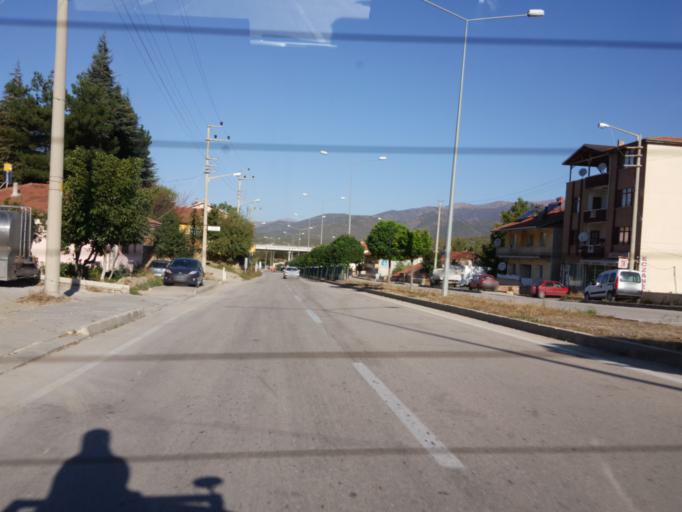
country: TR
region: Amasya
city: Ezinepazari
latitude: 40.5691
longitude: 36.1383
